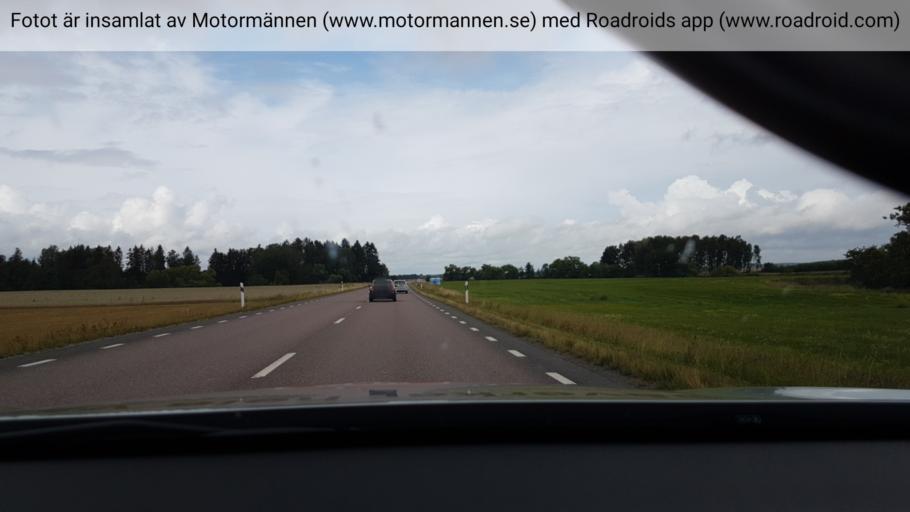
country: SE
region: Uppsala
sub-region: Uppsala Kommun
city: Gamla Uppsala
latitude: 59.8936
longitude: 17.5527
